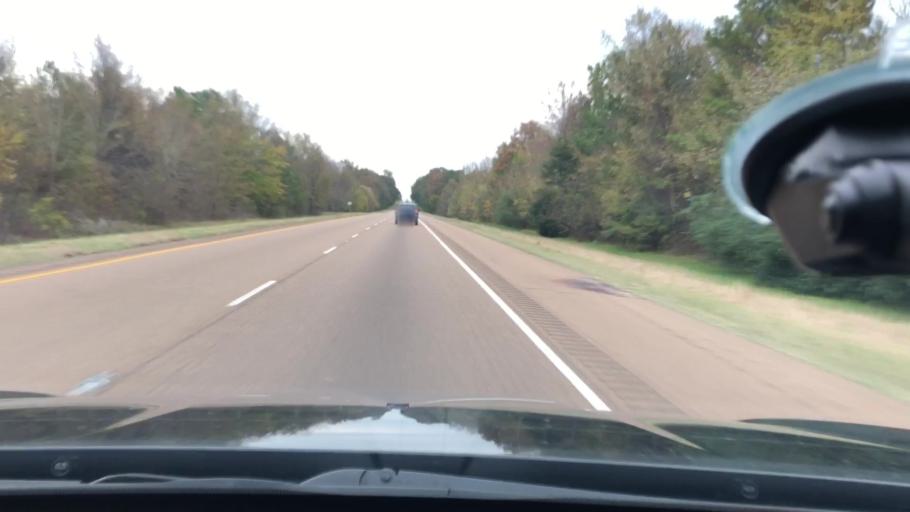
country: US
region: Arkansas
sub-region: Nevada County
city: Prescott
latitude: 33.7826
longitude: -93.4613
